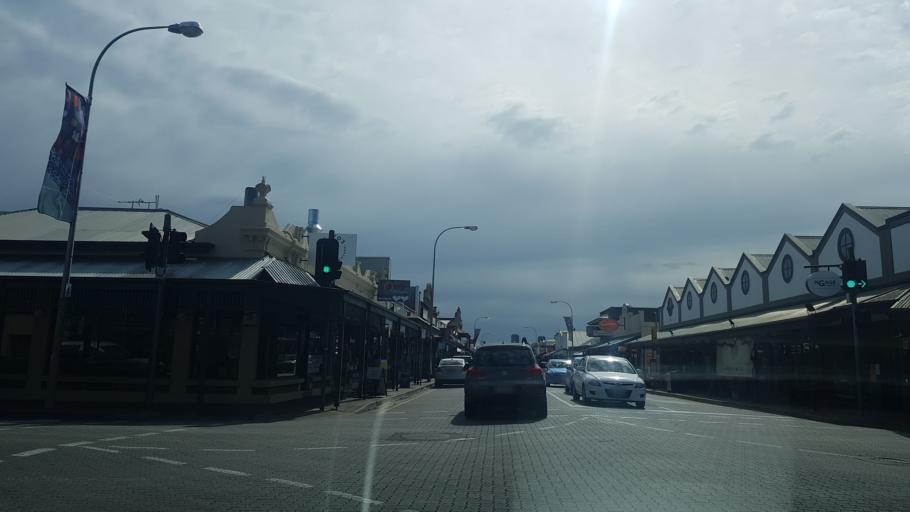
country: AU
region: South Australia
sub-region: Unley
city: Unley
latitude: -34.9553
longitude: 138.6001
